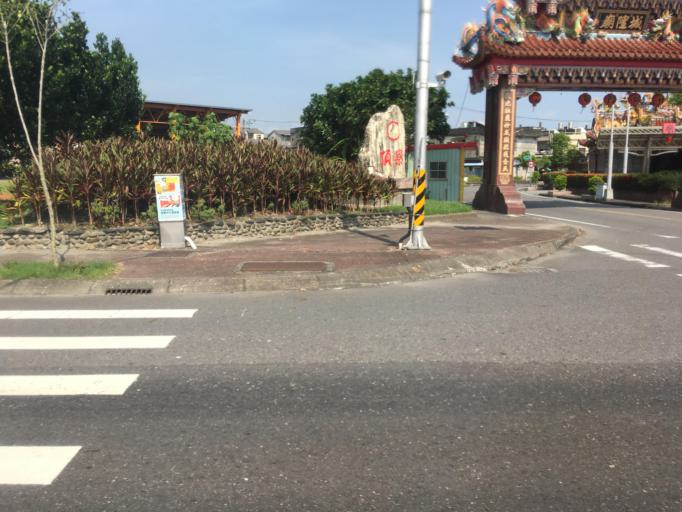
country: TW
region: Taiwan
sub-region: Yilan
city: Yilan
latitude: 24.6412
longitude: 121.8345
